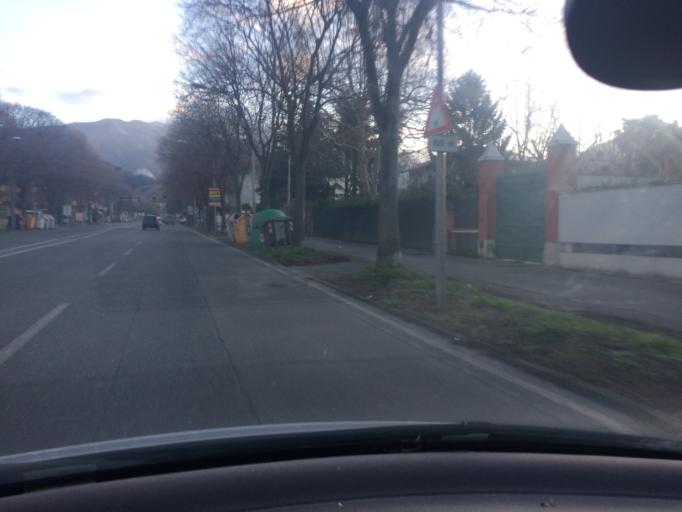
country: IT
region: Tuscany
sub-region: Provincia di Massa-Carrara
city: Carrara
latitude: 44.0617
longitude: 10.0706
